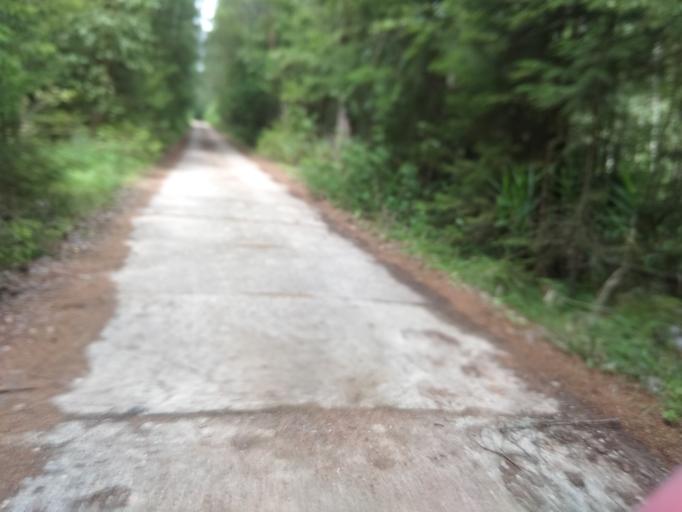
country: RU
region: Moskovskaya
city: Misheronskiy
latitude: 55.6163
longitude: 39.7222
